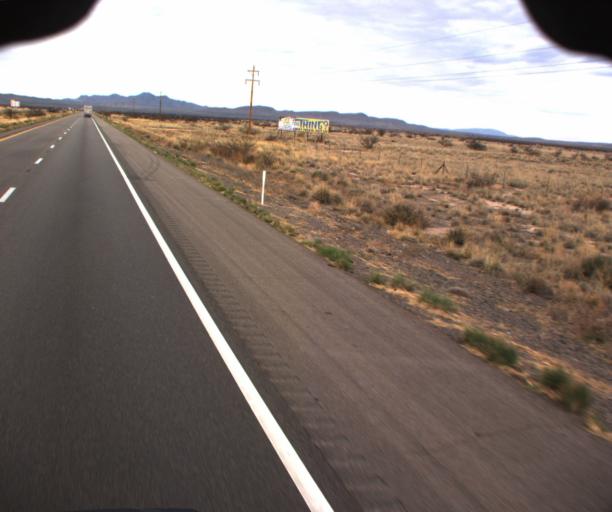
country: US
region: Arizona
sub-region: Cochise County
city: Willcox
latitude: 32.2097
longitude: -109.8939
